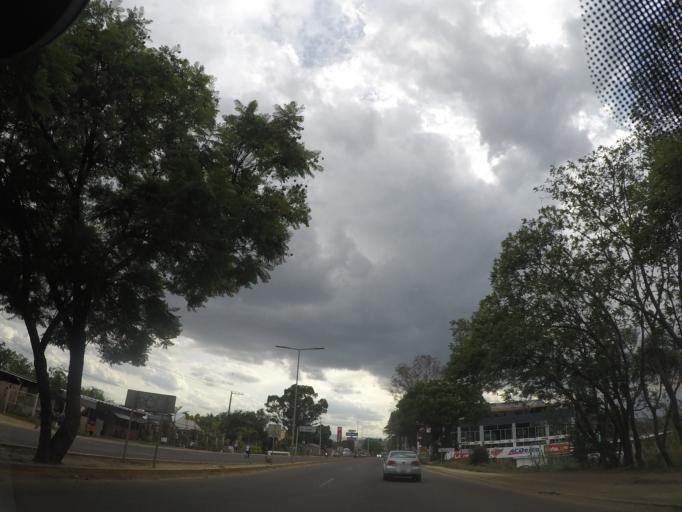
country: MX
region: Oaxaca
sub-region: Santa Cruz Amilpas
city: Santa Cruz Amilpas
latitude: 17.0686
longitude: -96.6915
